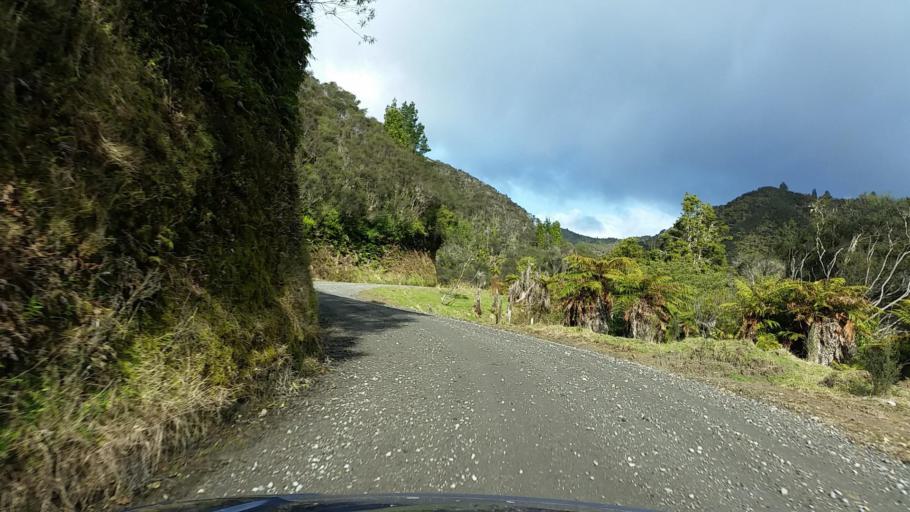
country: NZ
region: Taranaki
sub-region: South Taranaki District
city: Eltham
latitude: -39.2699
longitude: 174.7434
